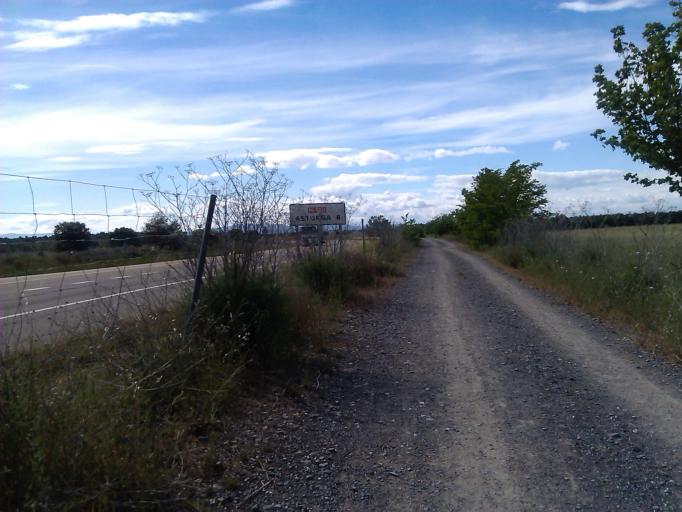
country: ES
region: Castille and Leon
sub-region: Provincia de Leon
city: San Justo de la Vega
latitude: 42.4517
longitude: -5.9861
